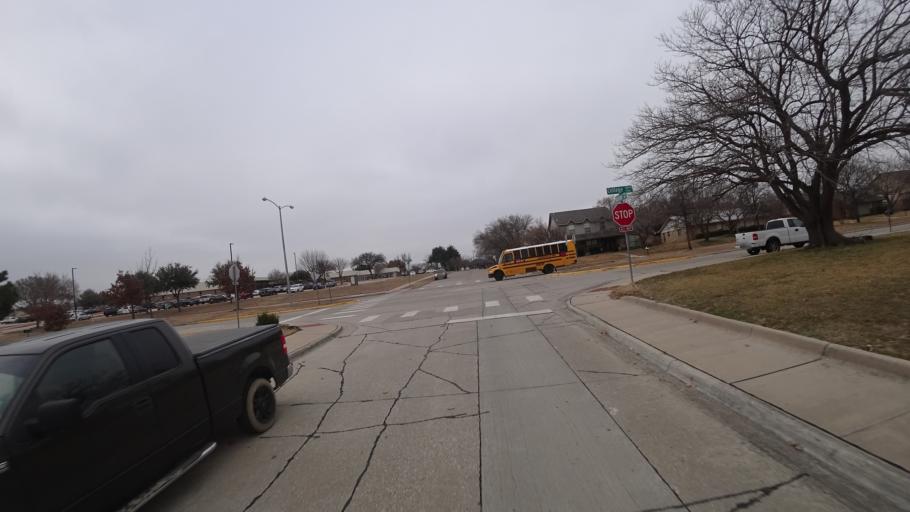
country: US
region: Texas
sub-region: Denton County
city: Highland Village
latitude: 33.0493
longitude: -97.0401
